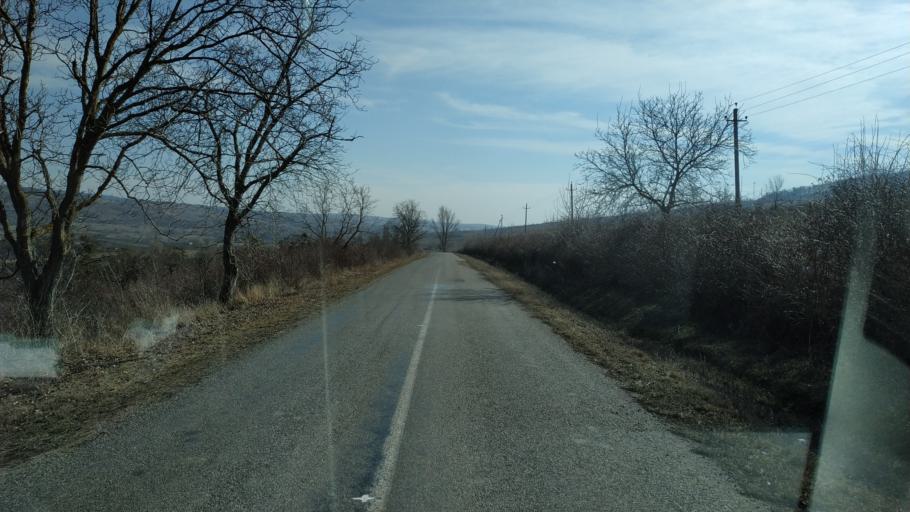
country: MD
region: Nisporeni
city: Nisporeni
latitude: 47.1752
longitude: 28.0865
